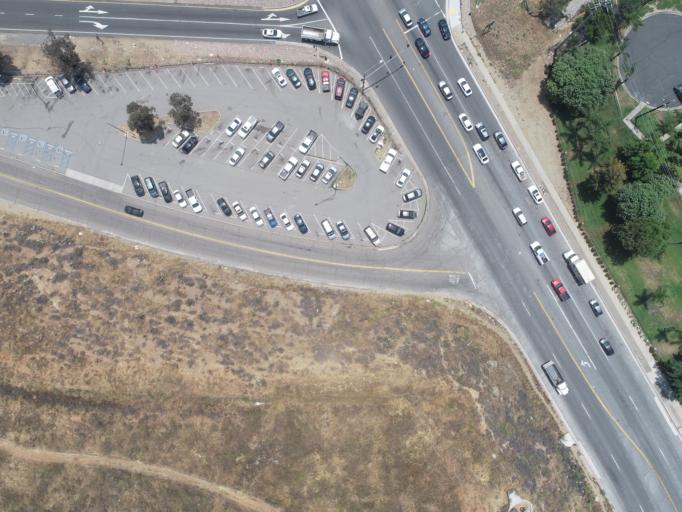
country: US
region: California
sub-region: Riverside County
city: Glen Avon
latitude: 34.0202
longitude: -117.5070
